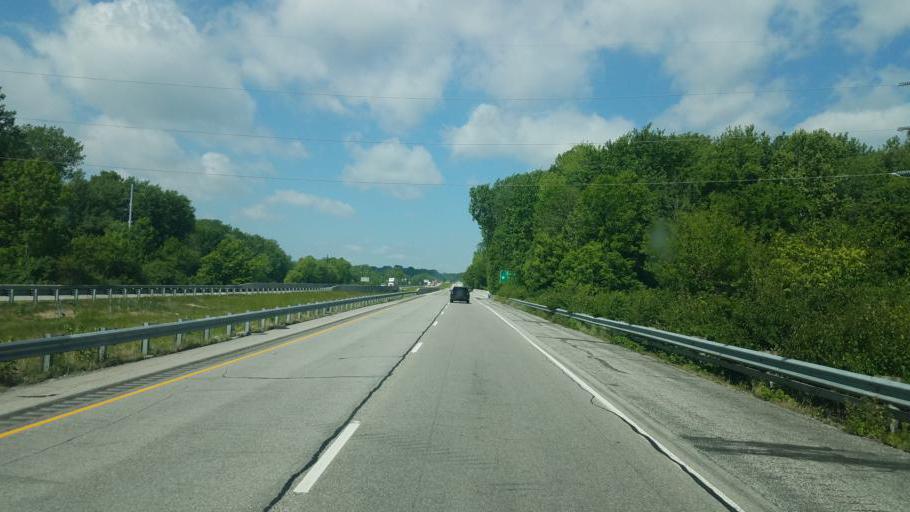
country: US
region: Indiana
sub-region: Vigo County
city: West Terre Haute
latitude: 39.4488
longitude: -87.4487
